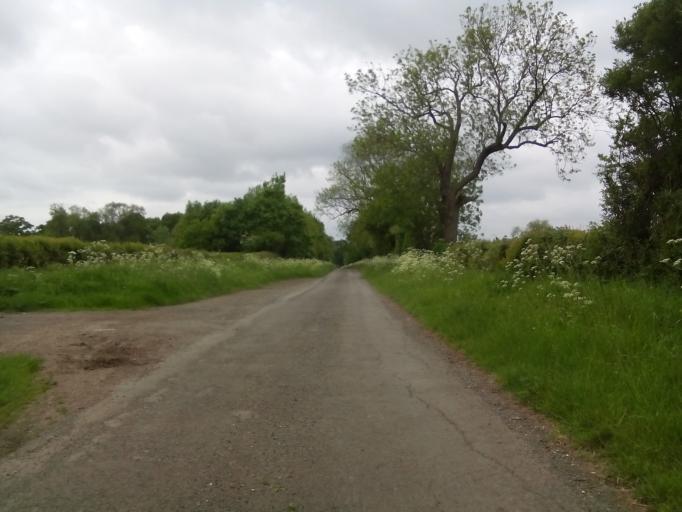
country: GB
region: England
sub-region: District of Rutland
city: South Luffenham
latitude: 52.5388
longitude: -0.5921
